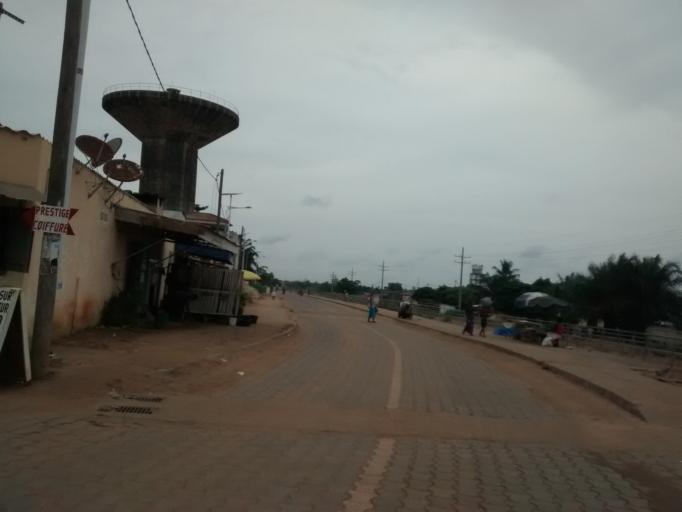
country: TG
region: Maritime
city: Lome
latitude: 6.1499
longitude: 1.2123
